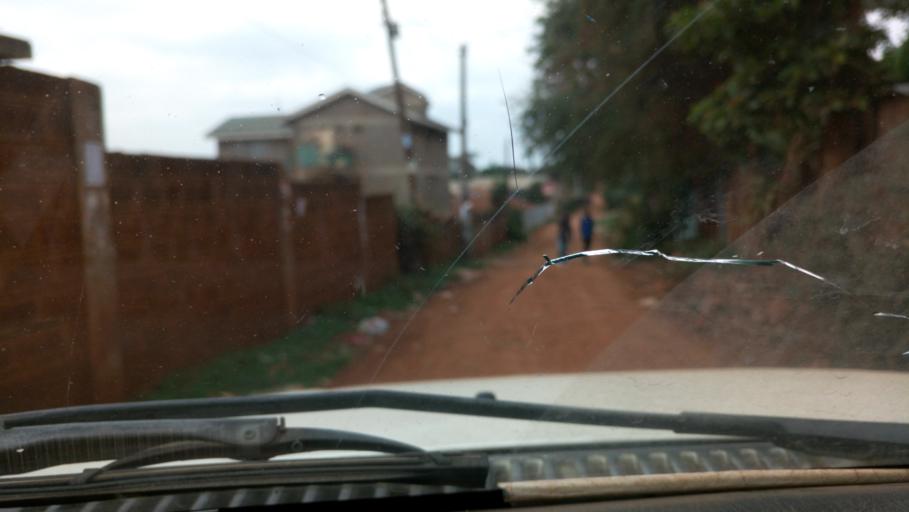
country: KE
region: Nairobi Area
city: Nairobi
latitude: -1.2898
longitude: 36.7358
